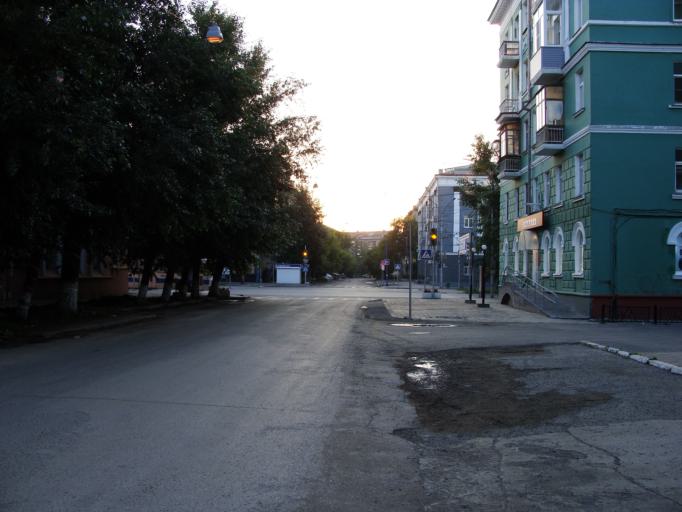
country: RU
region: Altai Krai
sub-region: Gorod Barnaulskiy
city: Barnaul
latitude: 53.3520
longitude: 83.7713
